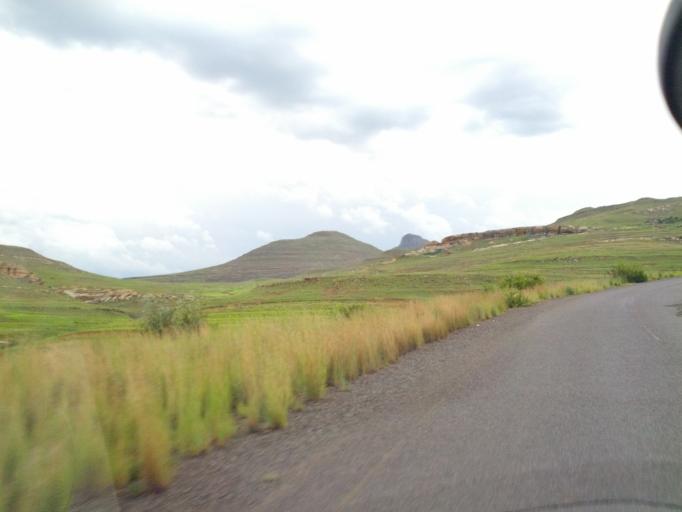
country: LS
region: Qacha's Nek
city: Qacha's Nek
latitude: -30.0715
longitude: 28.5979
